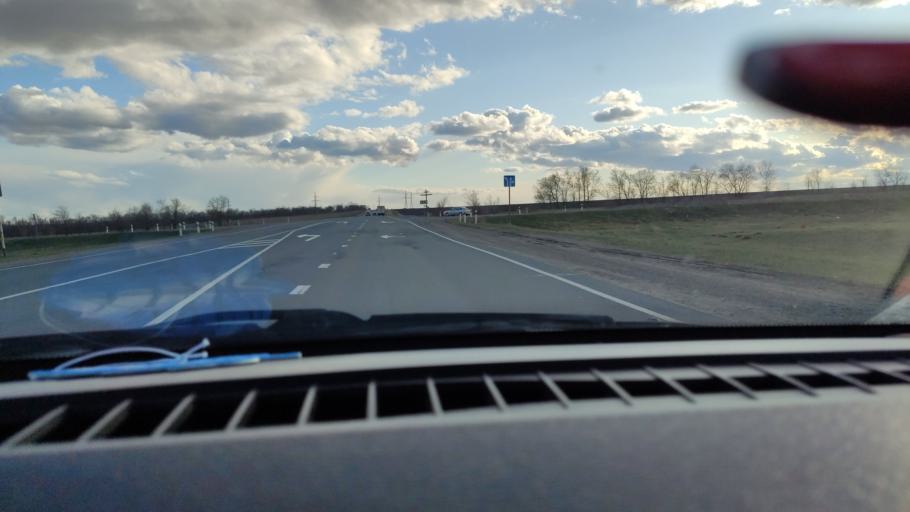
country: RU
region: Saratov
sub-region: Saratovskiy Rayon
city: Saratov
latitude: 51.7507
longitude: 46.0597
